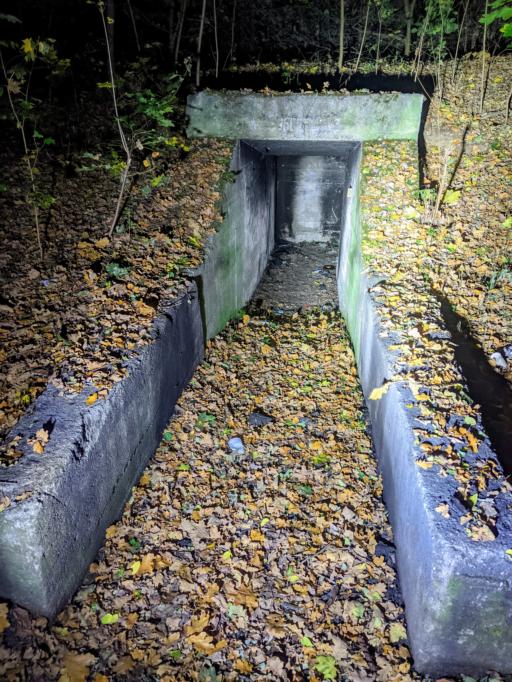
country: PL
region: Lubusz
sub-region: Powiat nowosolski
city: Nowa Sol
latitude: 51.7974
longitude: 15.7029
